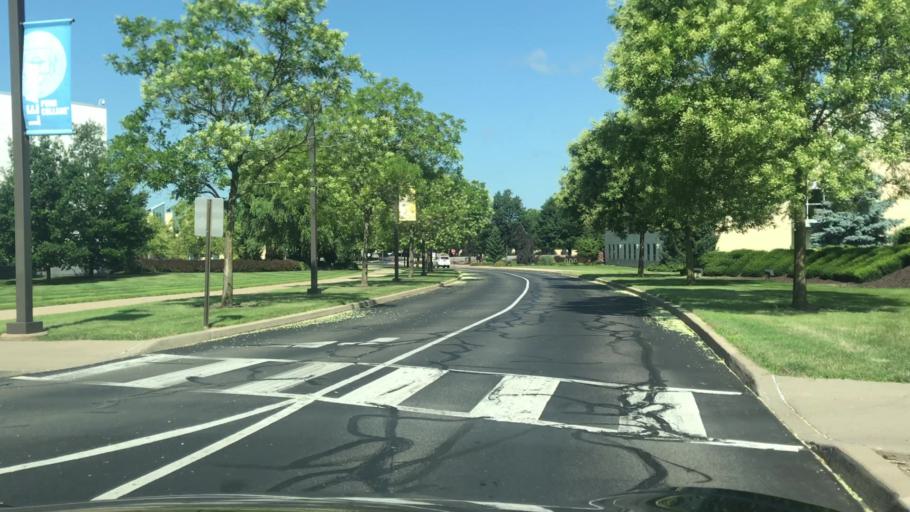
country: US
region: Pennsylvania
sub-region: Lycoming County
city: Duboistown
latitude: 41.2348
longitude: -77.0212
